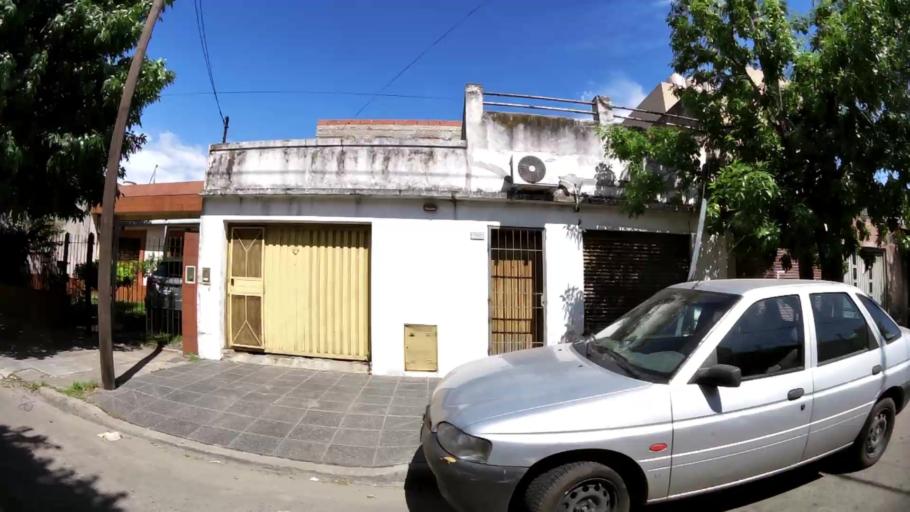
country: AR
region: Buenos Aires
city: San Justo
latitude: -34.6716
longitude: -58.5645
